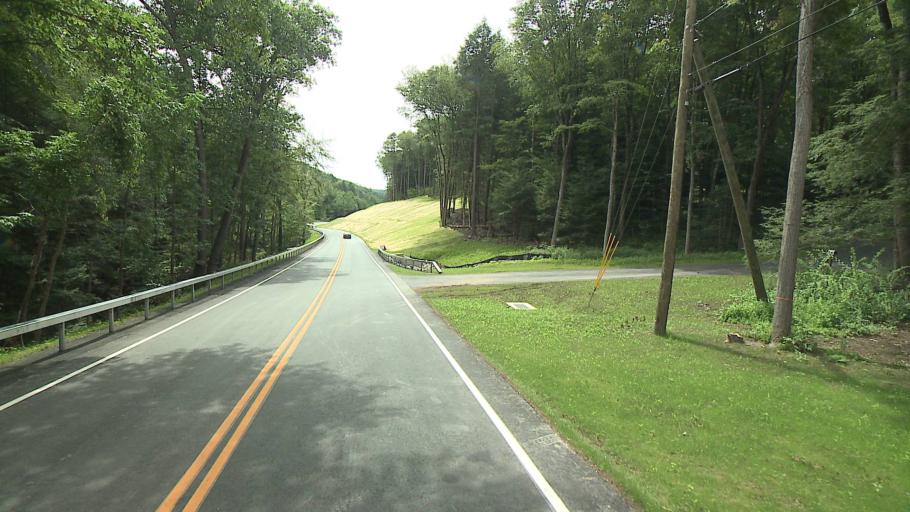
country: US
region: Connecticut
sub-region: Fairfield County
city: Newtown
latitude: 41.4924
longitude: -73.3529
